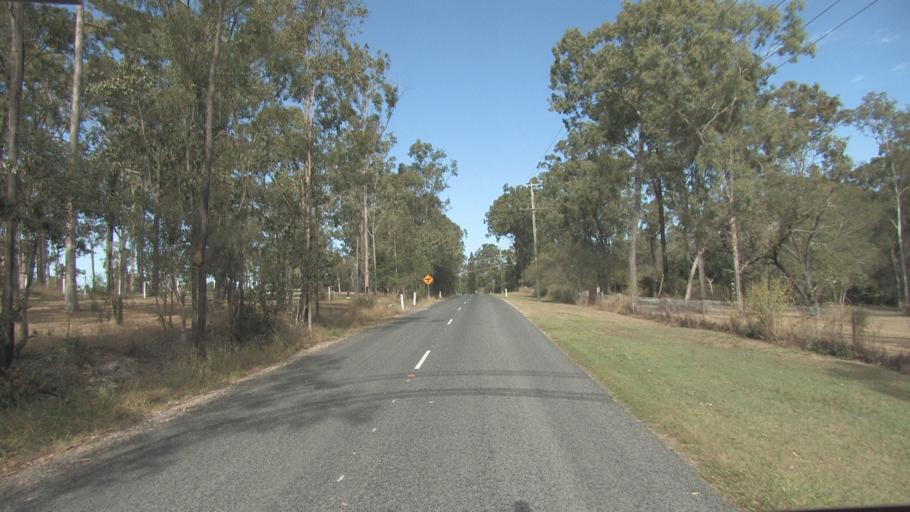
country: AU
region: Queensland
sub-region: Logan
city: North Maclean
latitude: -27.7634
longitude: 152.9703
